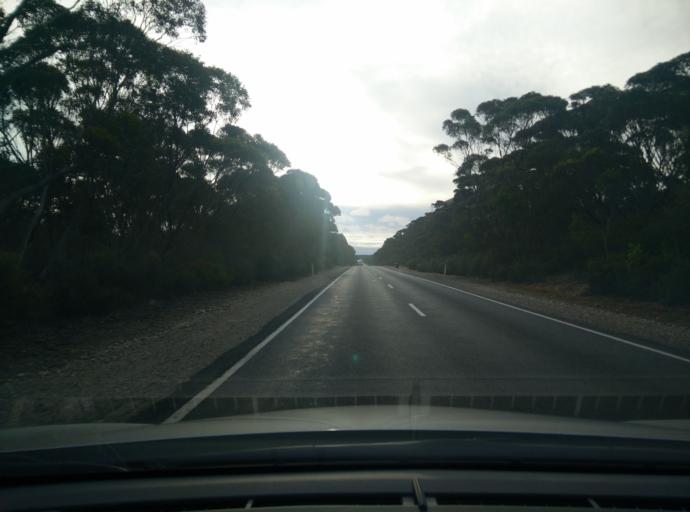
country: AU
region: South Australia
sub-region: Kangaroo Island
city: Kingscote
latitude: -35.7991
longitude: 137.8462
